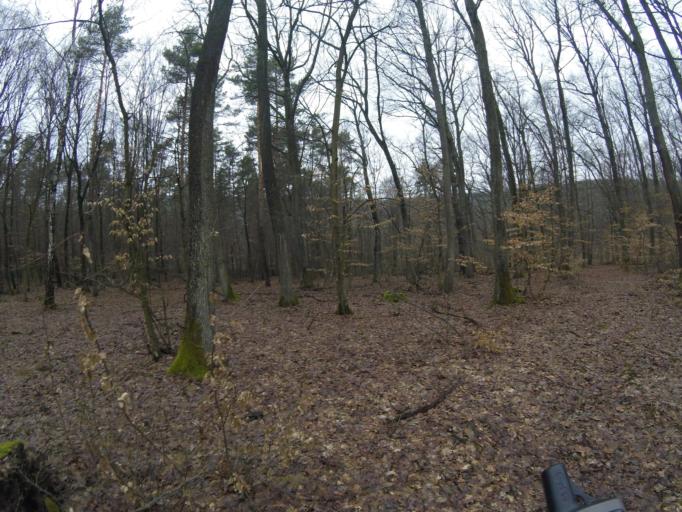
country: HU
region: Borsod-Abauj-Zemplen
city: Rudabanya
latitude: 48.4523
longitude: 20.5724
